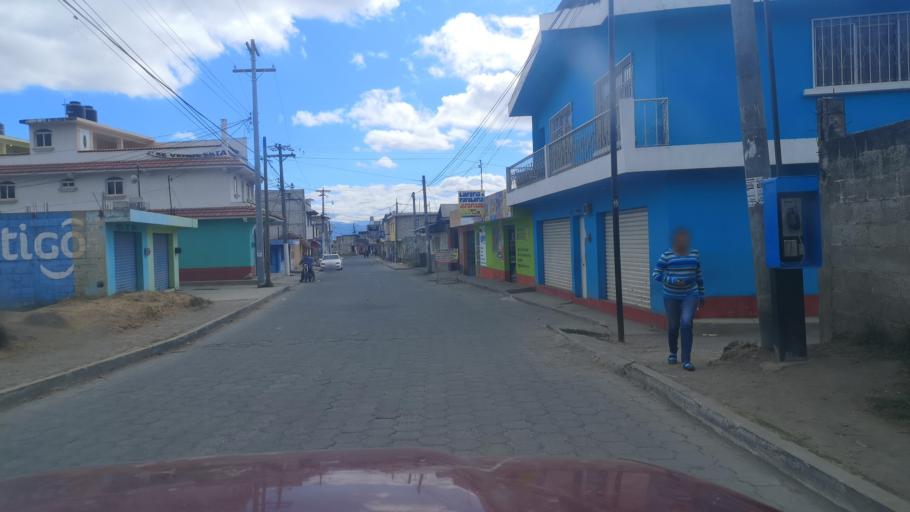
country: GT
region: Quetzaltenango
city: Quetzaltenango
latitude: 14.8367
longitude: -91.5398
